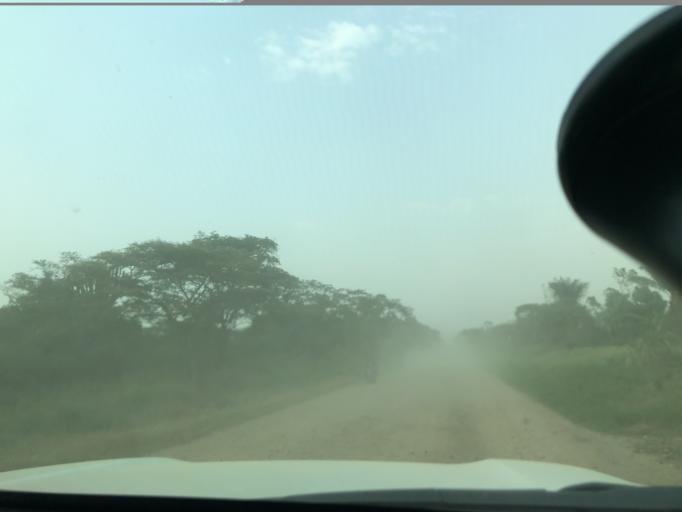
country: CD
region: Nord Kivu
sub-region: North Kivu
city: Butembo
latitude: 0.1538
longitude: 29.6415
